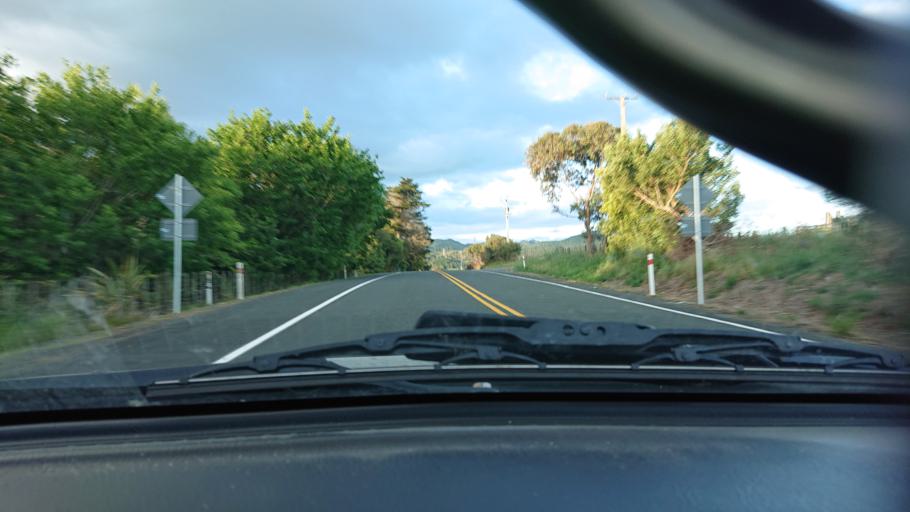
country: NZ
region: Auckland
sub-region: Auckland
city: Parakai
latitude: -36.5206
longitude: 174.4488
